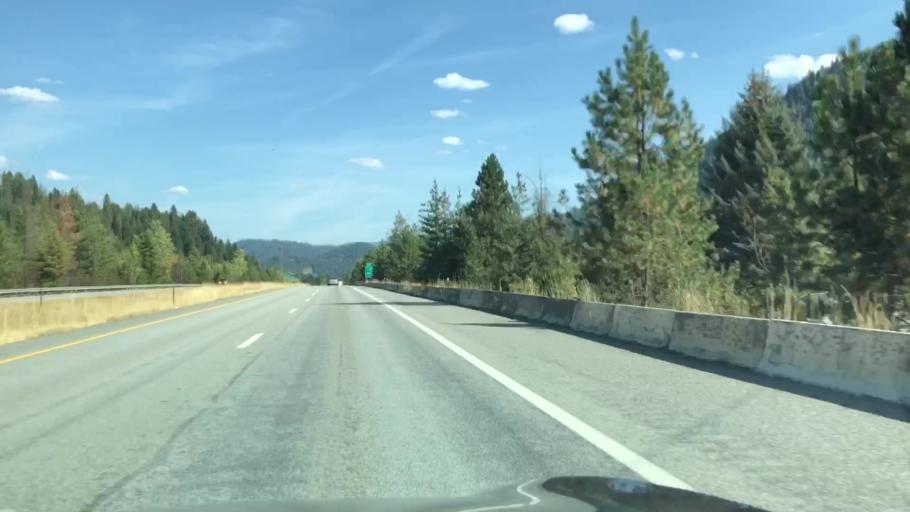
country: US
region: Idaho
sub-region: Shoshone County
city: Osburn
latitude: 47.5134
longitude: -116.0276
